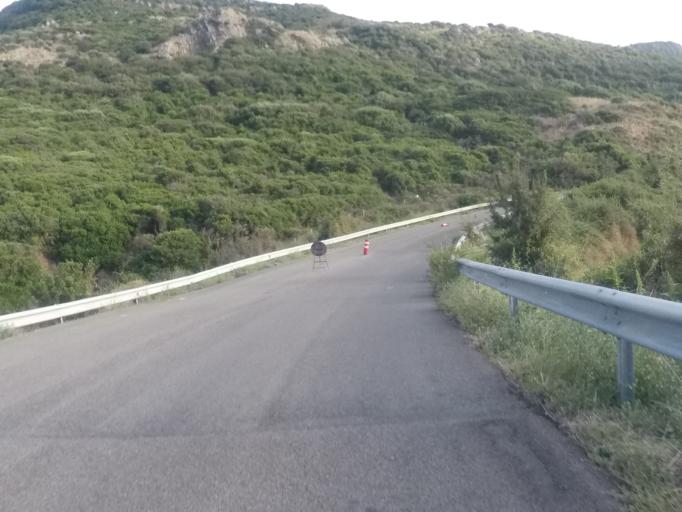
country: IT
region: Sardinia
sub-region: Provincia di Oristano
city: Montresta
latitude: 40.4065
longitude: 8.4135
